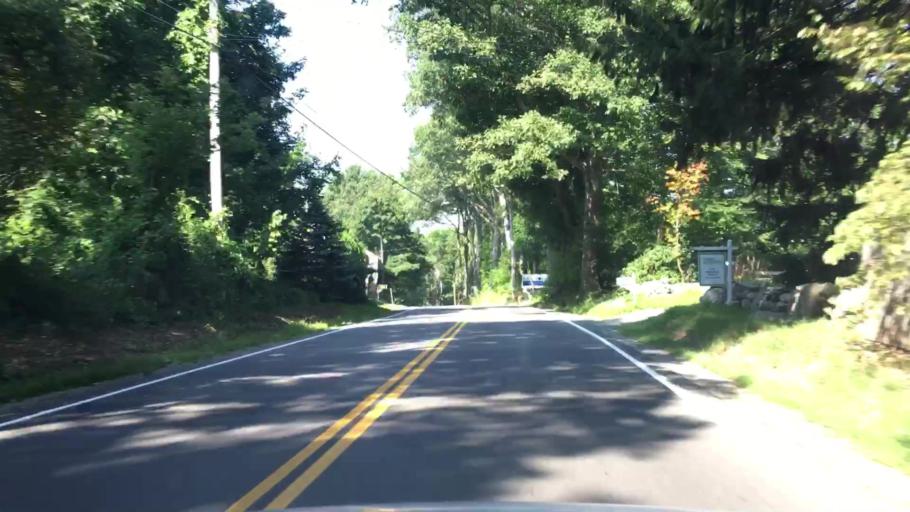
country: US
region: New Hampshire
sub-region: Rockingham County
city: Kensington
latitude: 42.9100
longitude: -70.9562
